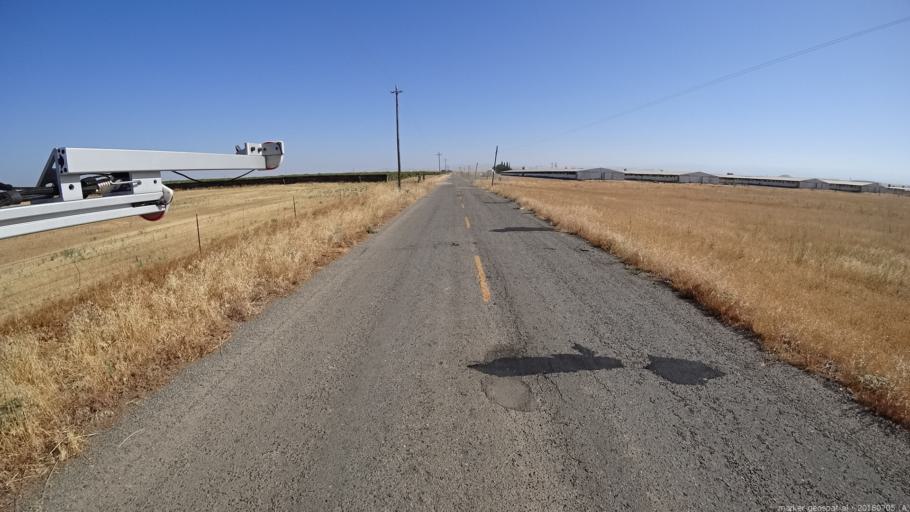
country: US
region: California
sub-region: Madera County
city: Madera Acres
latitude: 37.1478
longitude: -120.0748
